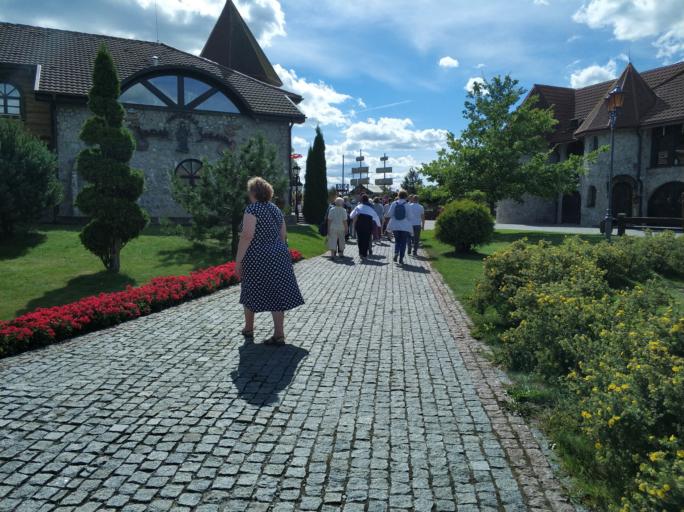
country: BY
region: Grodnenskaya
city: Hrodna
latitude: 53.5990
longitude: 23.7390
